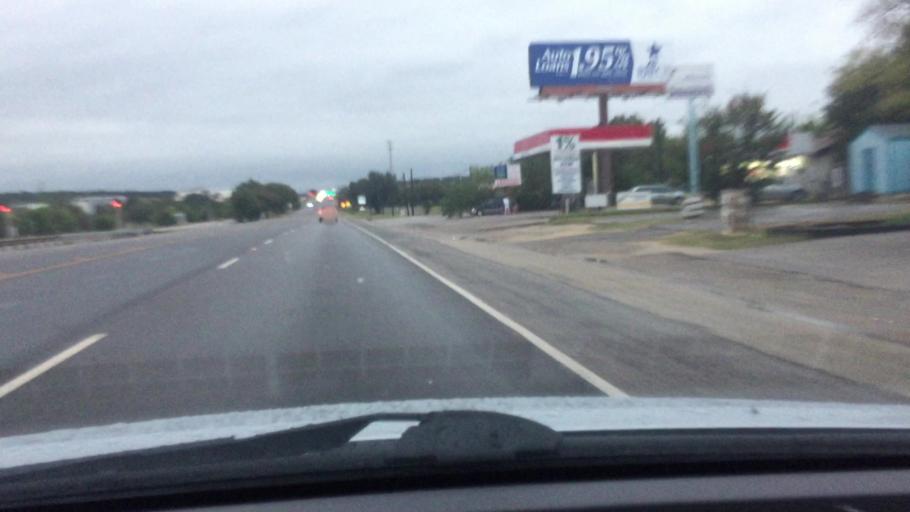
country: US
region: Texas
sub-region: Williamson County
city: Leander
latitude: 30.5760
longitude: -97.8518
